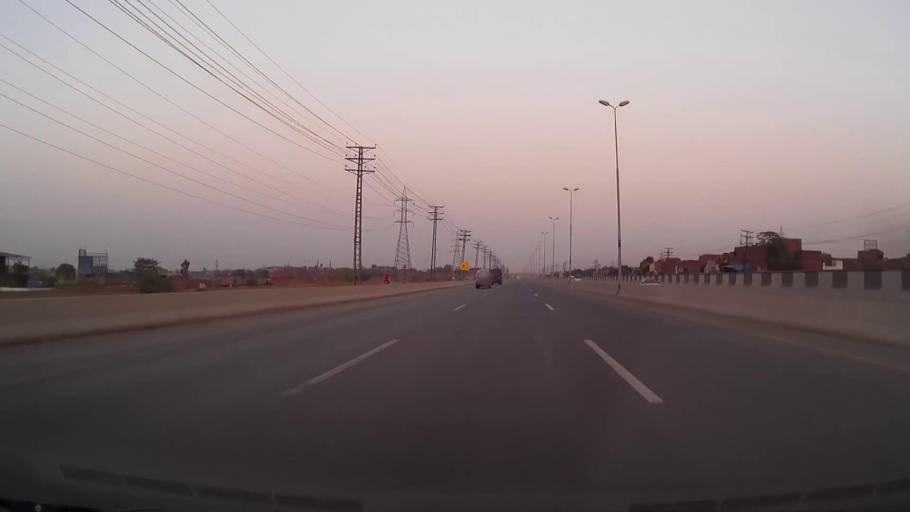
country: PK
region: Punjab
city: Lahore
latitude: 31.6095
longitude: 74.3297
